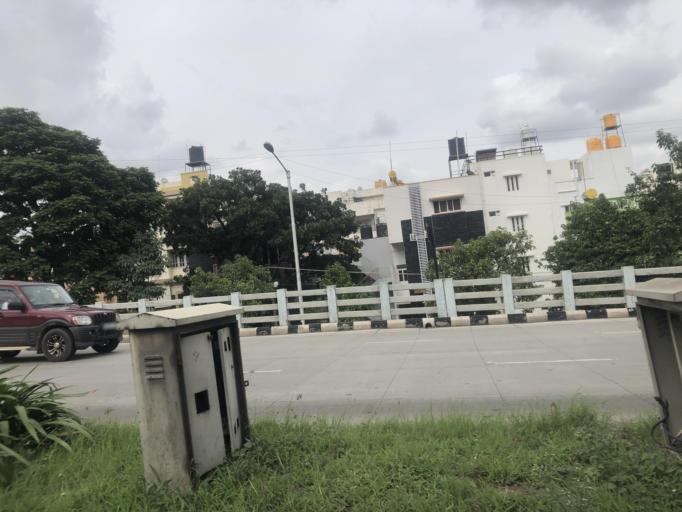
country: IN
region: Karnataka
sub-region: Bangalore Urban
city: Bangalore
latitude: 12.9665
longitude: 77.5125
